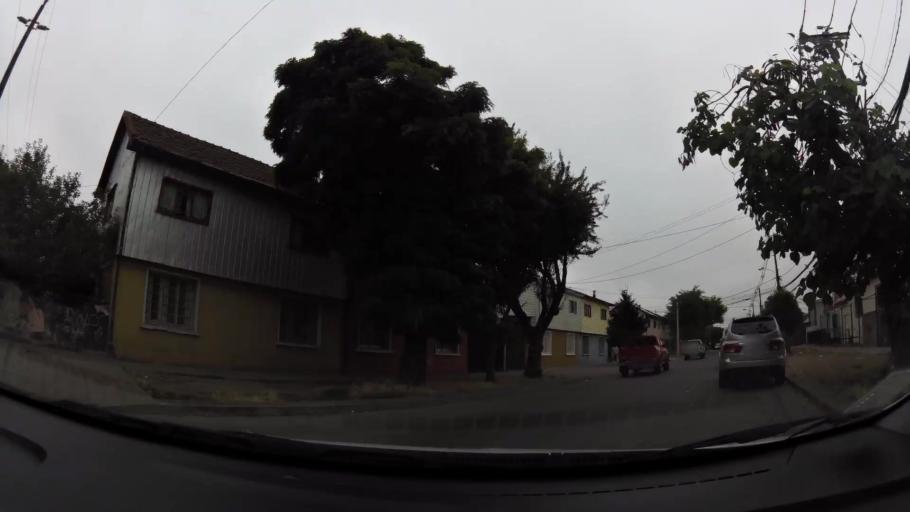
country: CL
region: Biobio
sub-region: Provincia de Concepcion
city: Concepcion
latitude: -36.8105
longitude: -73.0350
